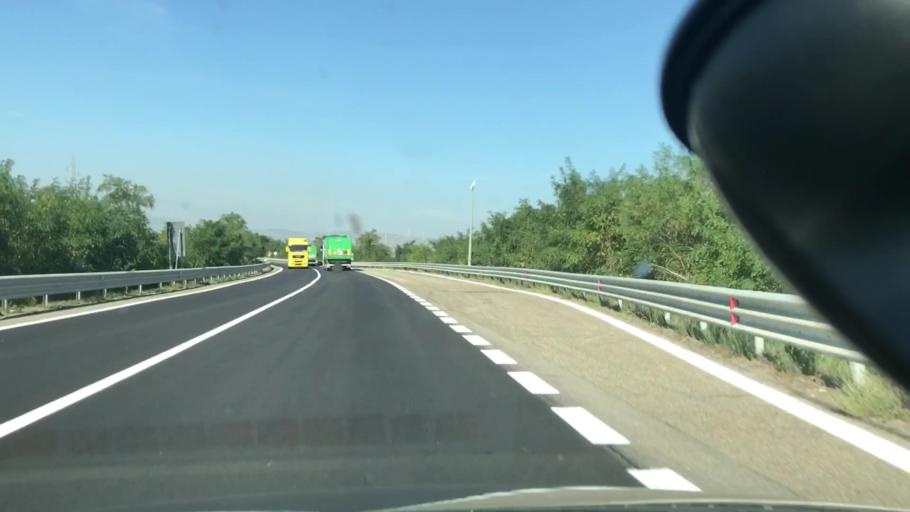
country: IT
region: Basilicate
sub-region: Provincia di Potenza
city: Zona 179
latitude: 41.0823
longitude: 15.6233
